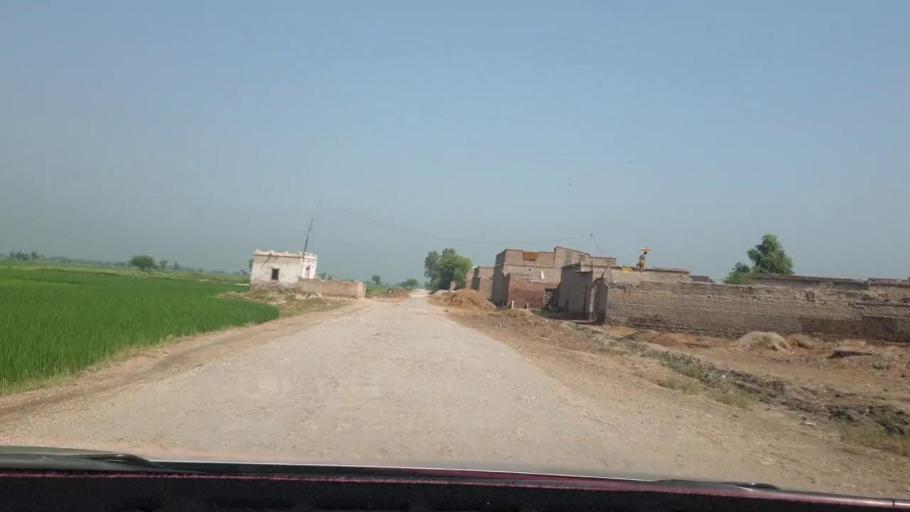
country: PK
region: Sindh
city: Nasirabad
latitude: 27.4248
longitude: 67.9051
